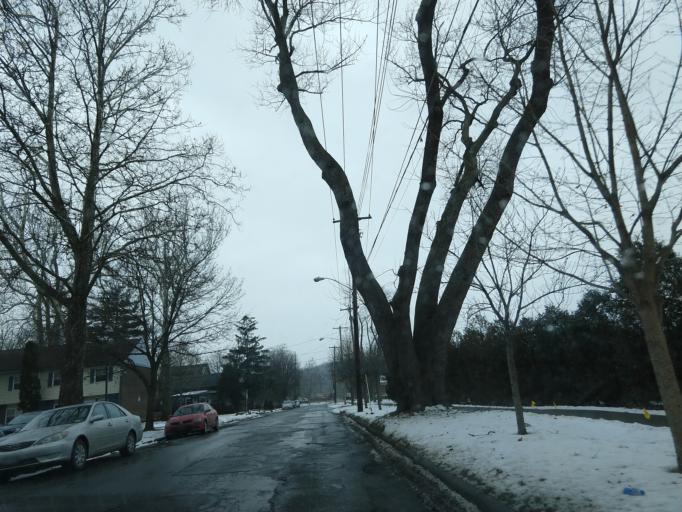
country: US
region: New York
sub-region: Tompkins County
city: Ithaca
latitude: 42.4459
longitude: -76.5065
